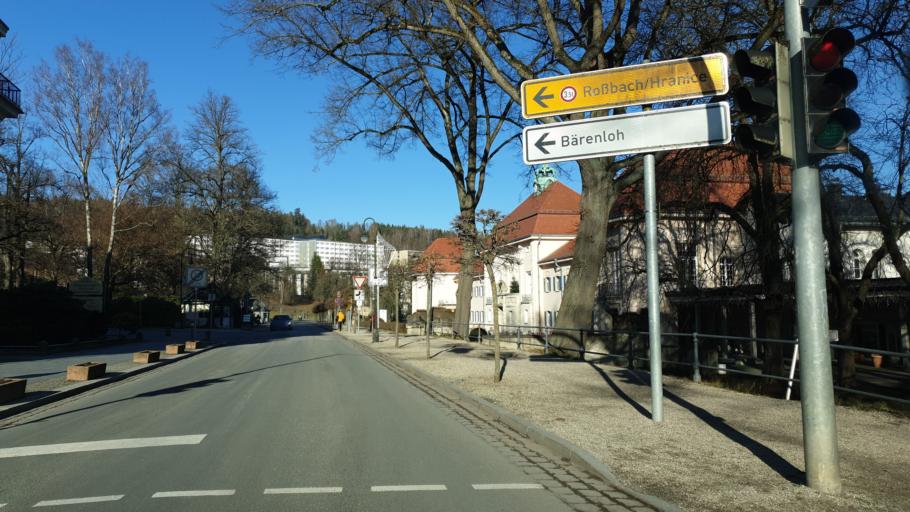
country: DE
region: Saxony
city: Bad Elster
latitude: 50.2822
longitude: 12.2394
